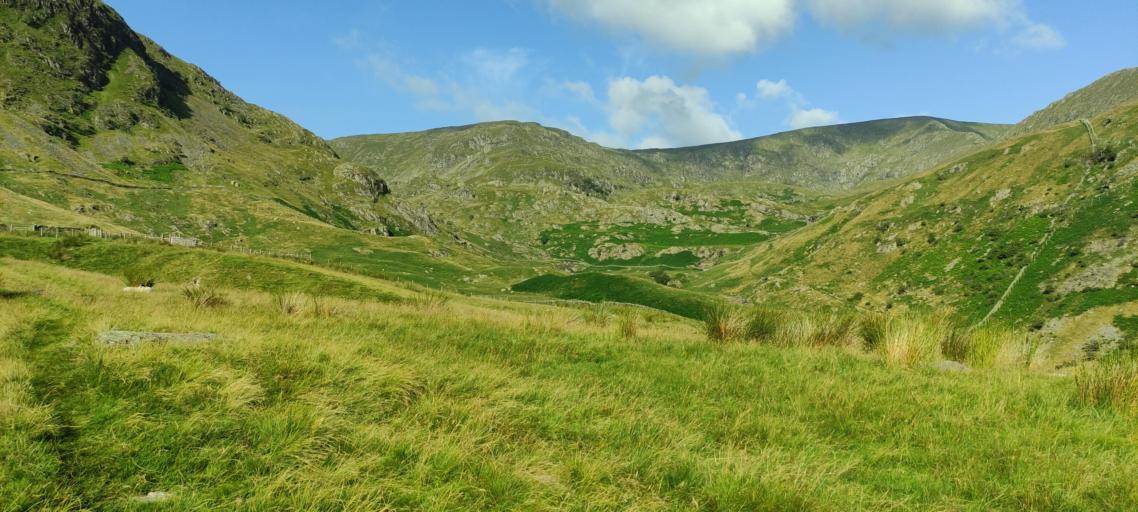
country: GB
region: England
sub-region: Cumbria
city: Windermere
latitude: 54.4878
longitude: -2.8223
